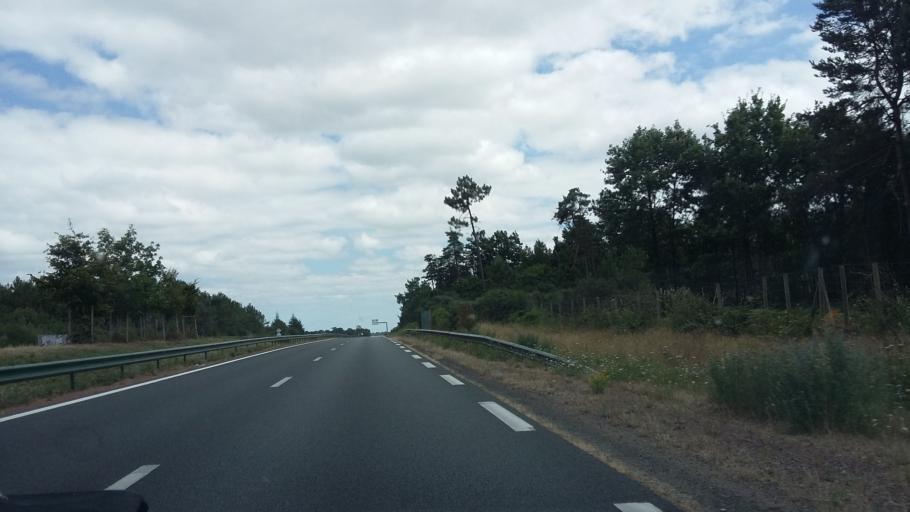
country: FR
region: Pays de la Loire
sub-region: Departement de la Vendee
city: Bournezeau
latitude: 46.6474
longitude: -1.2116
